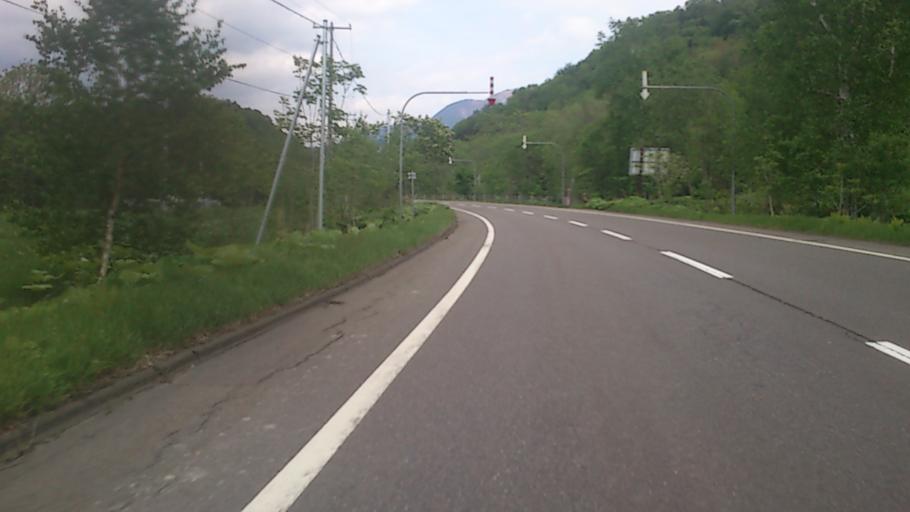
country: JP
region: Hokkaido
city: Kitami
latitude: 43.3826
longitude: 143.9104
